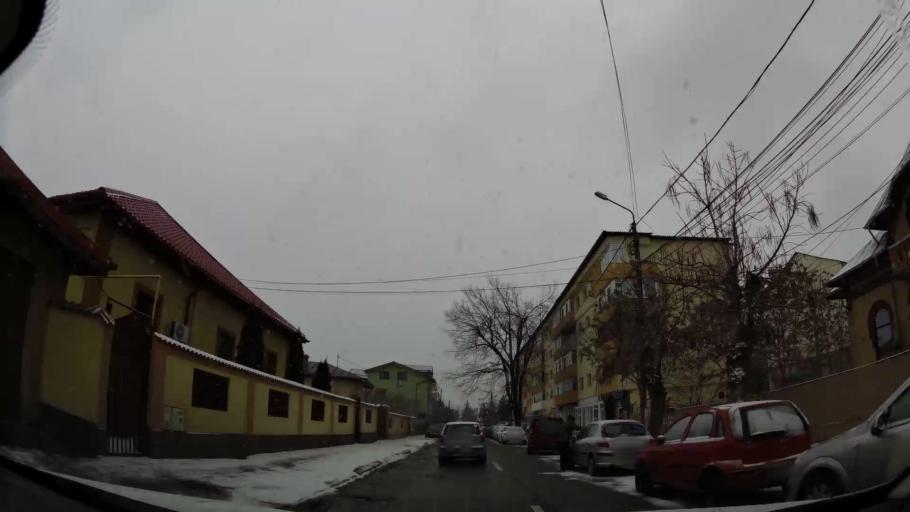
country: RO
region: Dambovita
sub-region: Municipiul Targoviste
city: Targoviste
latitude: 44.9311
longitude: 25.4537
